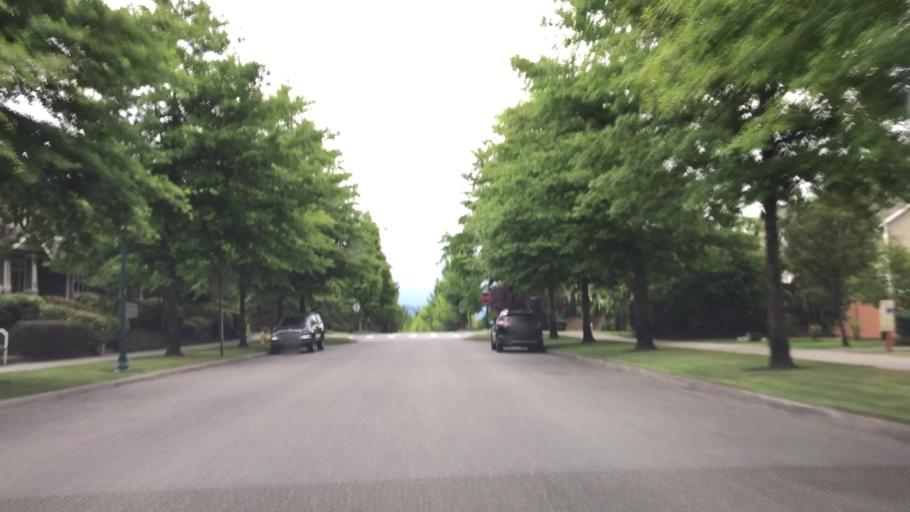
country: US
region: Washington
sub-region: King County
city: Fall City
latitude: 47.5340
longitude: -121.8690
